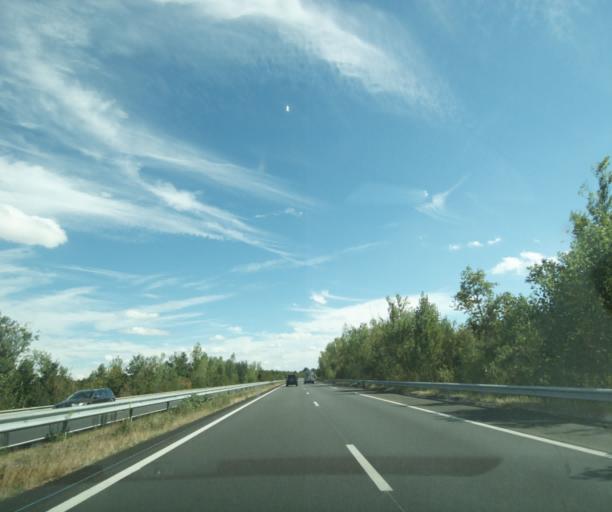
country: FR
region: Midi-Pyrenees
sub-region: Departement du Tarn-et-Garonne
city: Montech
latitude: 43.9803
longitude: 1.2548
